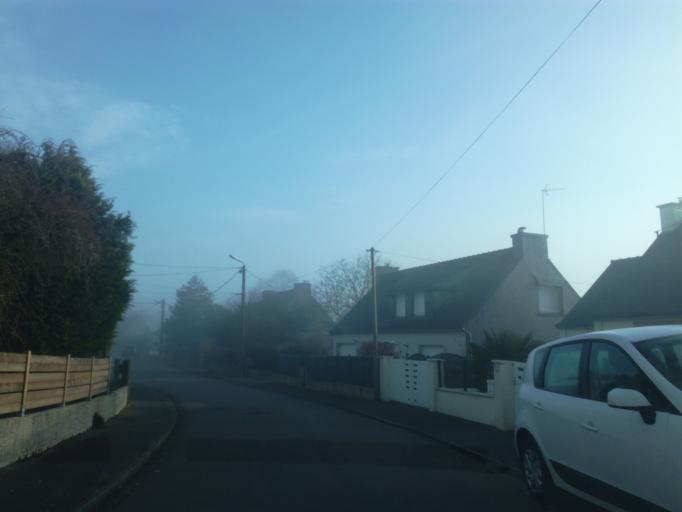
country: FR
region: Brittany
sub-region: Departement du Morbihan
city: Le Sourn
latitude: 48.0394
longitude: -2.9826
